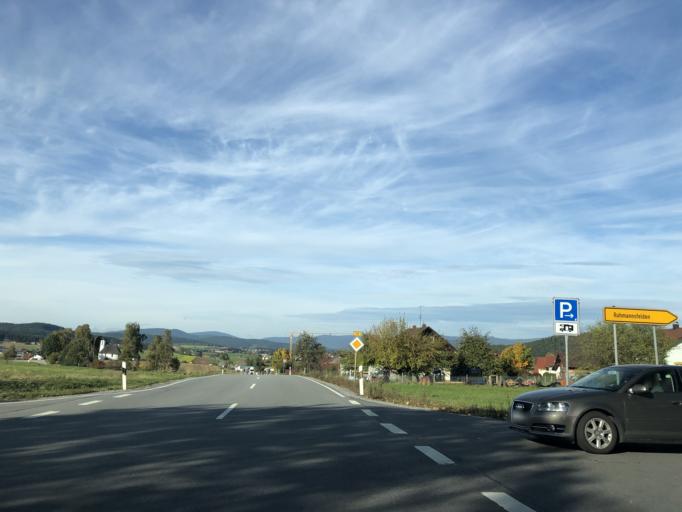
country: DE
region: Bavaria
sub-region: Lower Bavaria
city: Ruhmannsfelden
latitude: 48.9773
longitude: 12.9807
